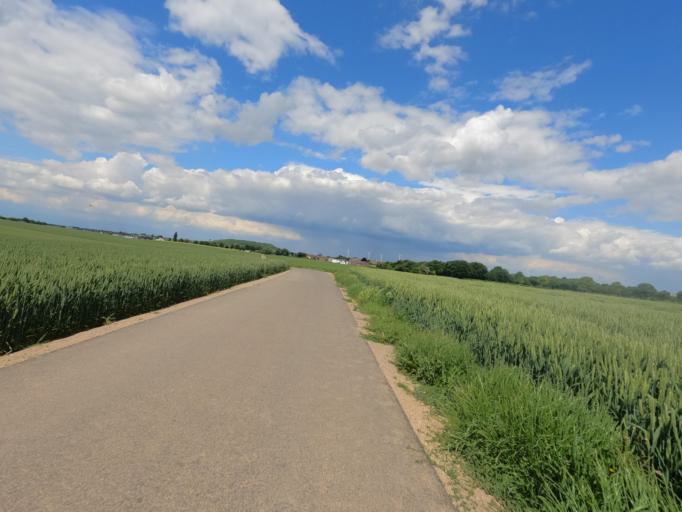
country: DE
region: North Rhine-Westphalia
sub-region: Regierungsbezirk Koln
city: Ubach-Palenberg
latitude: 50.9069
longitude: 6.1285
